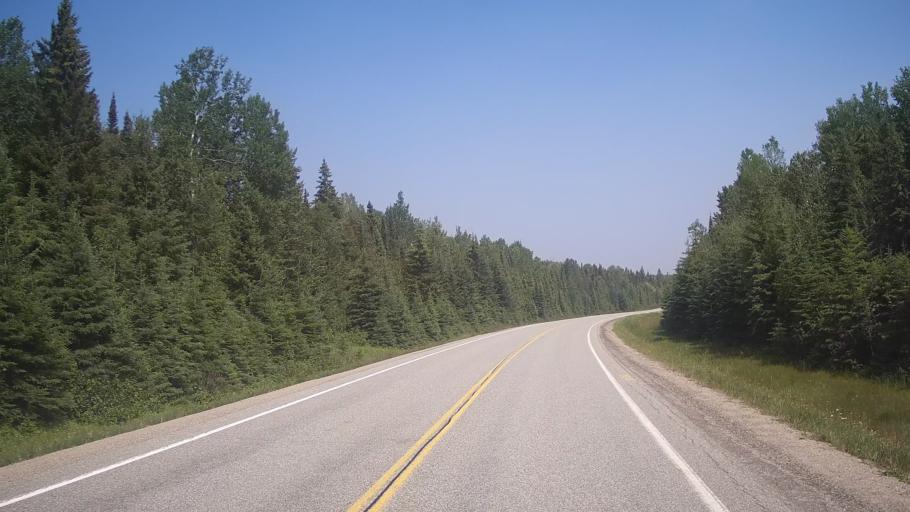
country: CA
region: Ontario
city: Timmins
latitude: 48.2336
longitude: -81.5763
